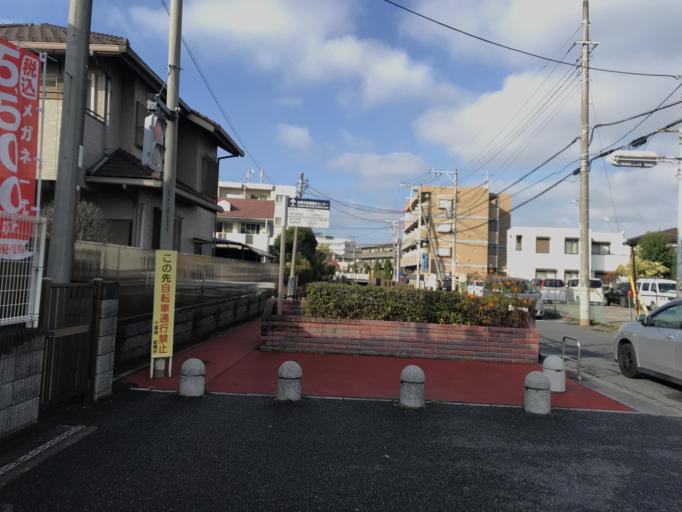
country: JP
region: Chiba
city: Funabashi
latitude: 35.7075
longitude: 139.9847
